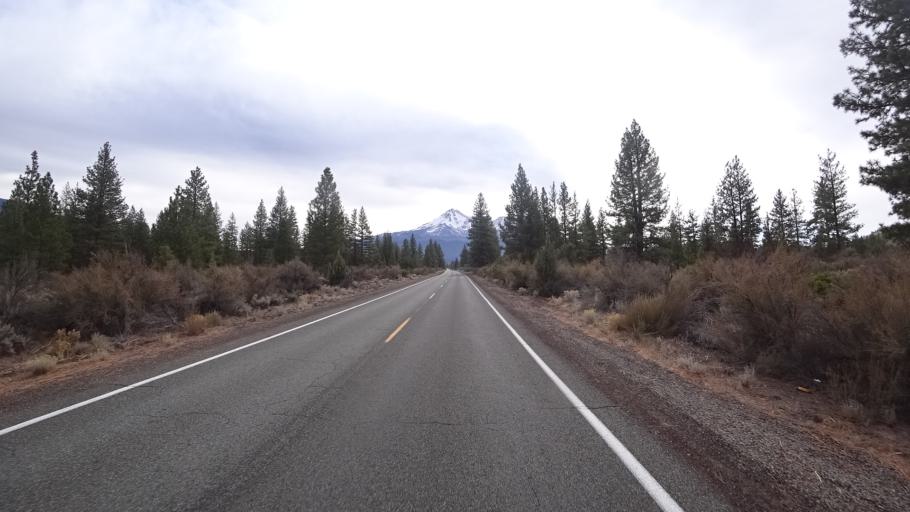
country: US
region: California
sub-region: Siskiyou County
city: Weed
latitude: 41.5473
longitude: -122.2479
